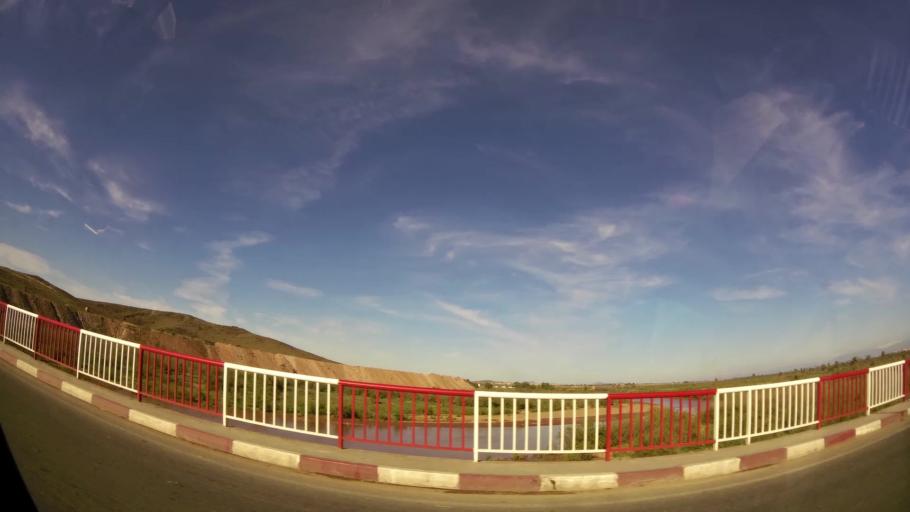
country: MA
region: Marrakech-Tensift-Al Haouz
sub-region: Marrakech
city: Marrakesh
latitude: 31.7006
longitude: -8.0608
